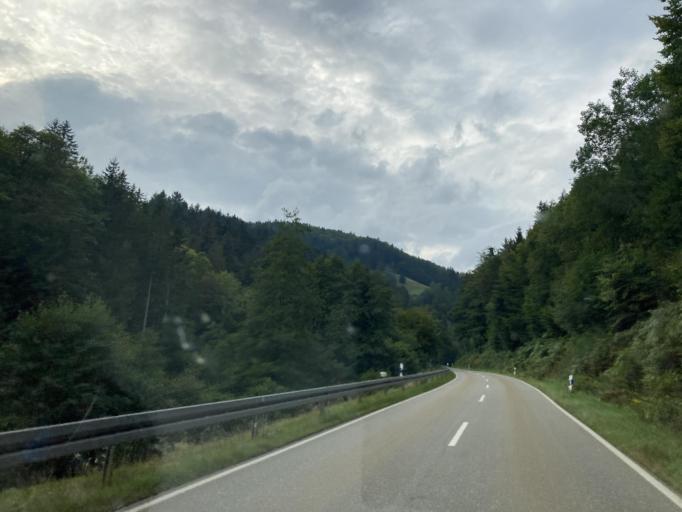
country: DE
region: Baden-Wuerttemberg
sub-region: Freiburg Region
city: Bollen
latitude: 47.7836
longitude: 7.8596
